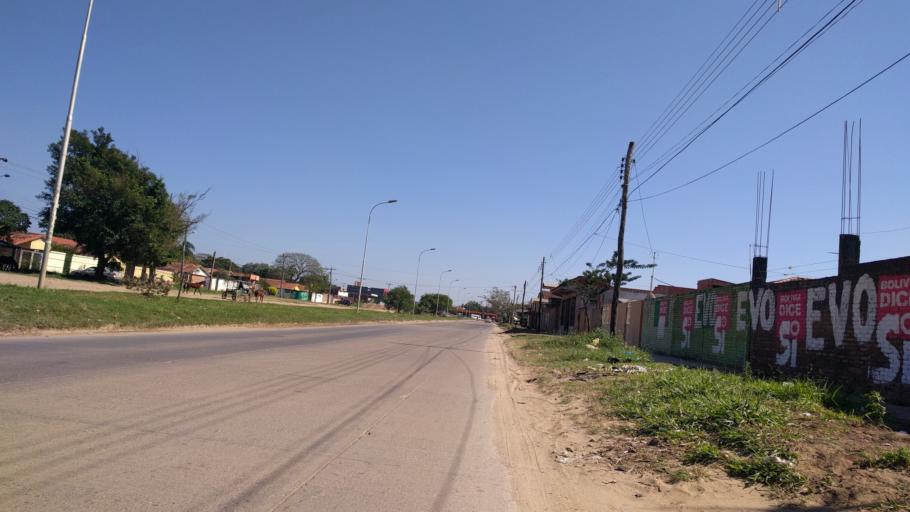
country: BO
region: Santa Cruz
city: Santa Cruz de la Sierra
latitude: -17.8534
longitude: -63.1957
